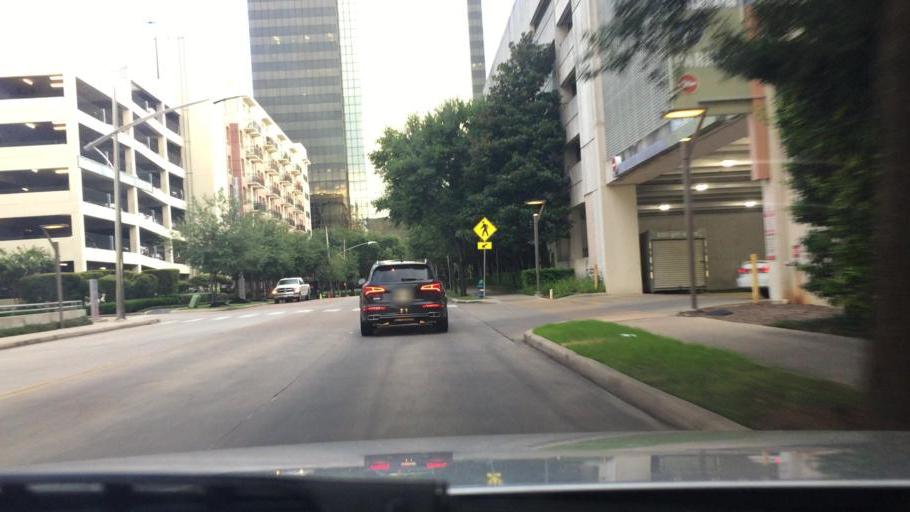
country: US
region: Texas
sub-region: Harris County
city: Bellaire
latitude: 29.7372
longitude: -95.4629
